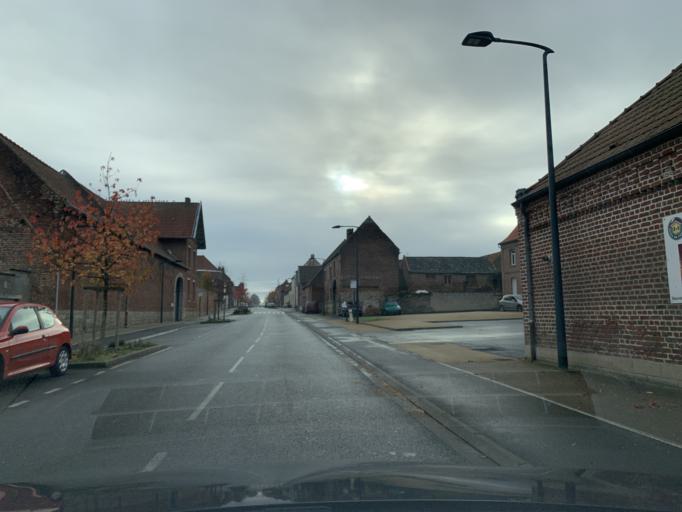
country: FR
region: Nord-Pas-de-Calais
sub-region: Departement du Nord
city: Cantin
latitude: 50.3098
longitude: 3.1271
